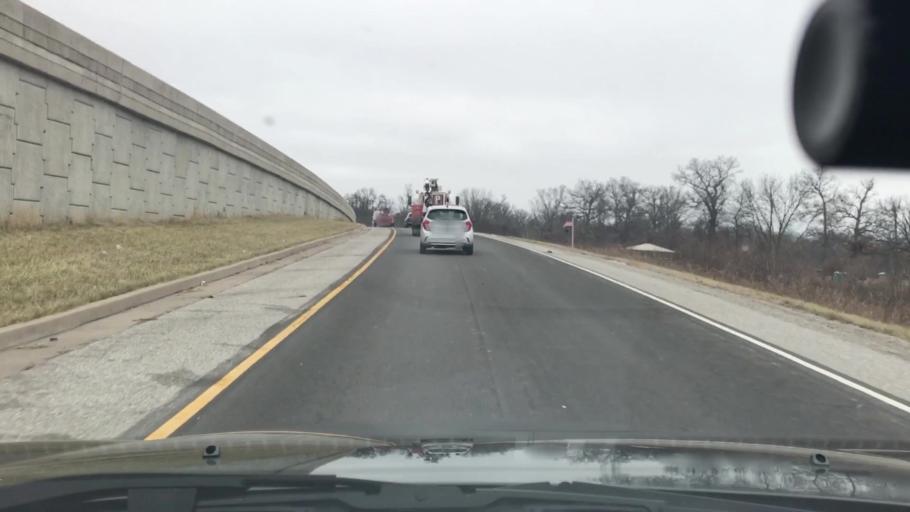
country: US
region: Illinois
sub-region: Madison County
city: Rosewood Heights
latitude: 38.9014
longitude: -90.0657
